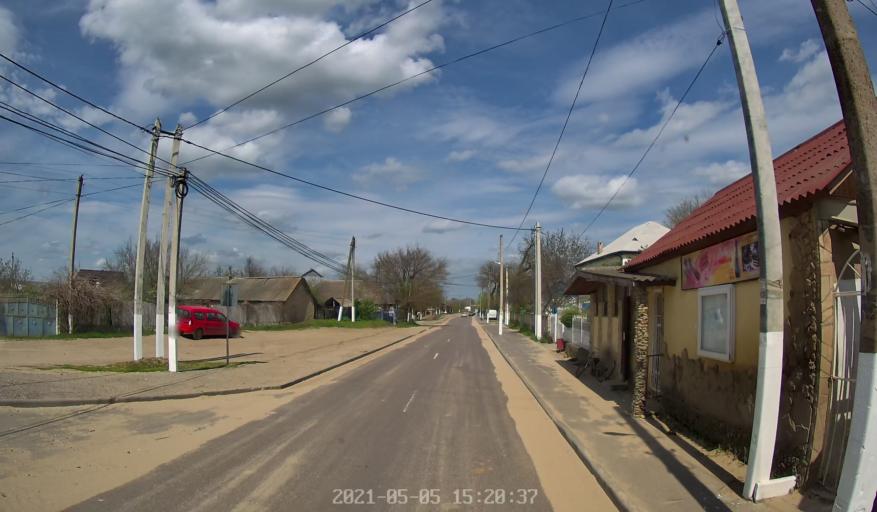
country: MD
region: Criuleni
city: Criuleni
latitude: 47.1321
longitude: 29.1996
